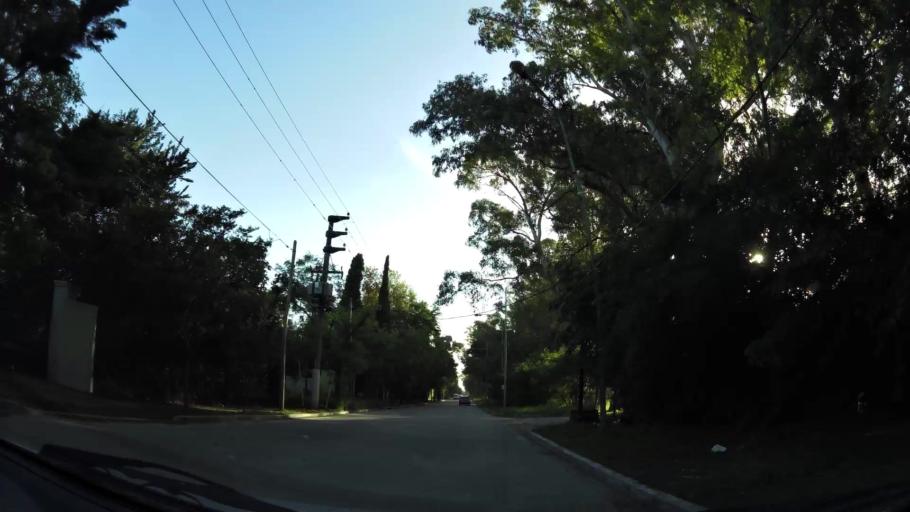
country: AR
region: Buenos Aires
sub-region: Partido de Quilmes
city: Quilmes
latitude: -34.8000
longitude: -58.1996
